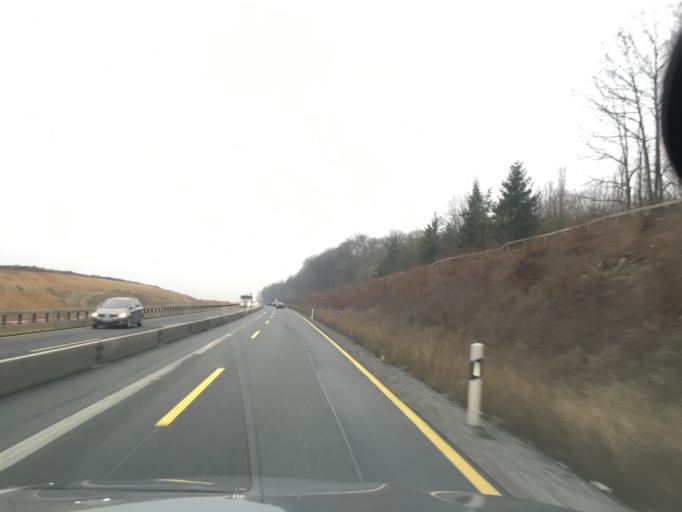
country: DE
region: Bavaria
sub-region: Regierungsbezirk Unterfranken
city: Holzkirchen
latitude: 49.7678
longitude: 9.6680
